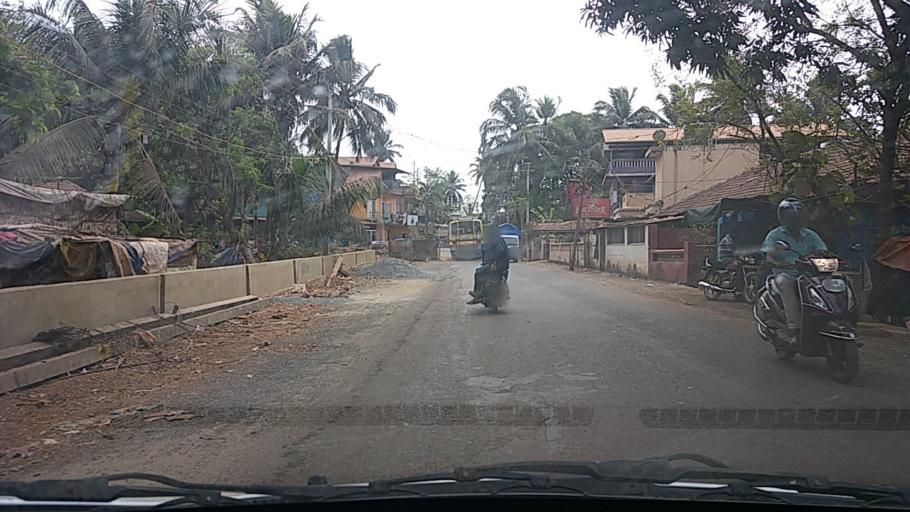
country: IN
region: Goa
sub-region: North Goa
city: Panaji
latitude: 15.5071
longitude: 73.8318
